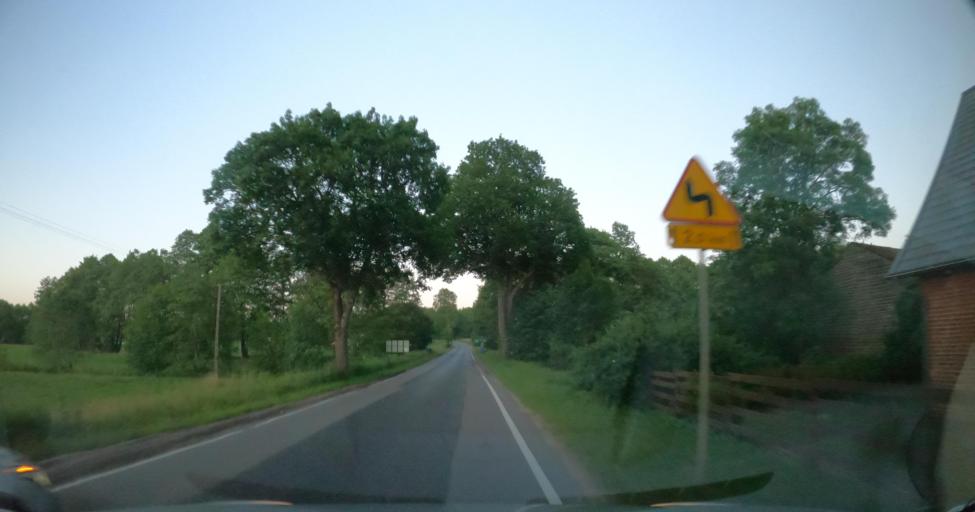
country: PL
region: Pomeranian Voivodeship
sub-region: Powiat wejherowski
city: Luzino
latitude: 54.4665
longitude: 18.0975
